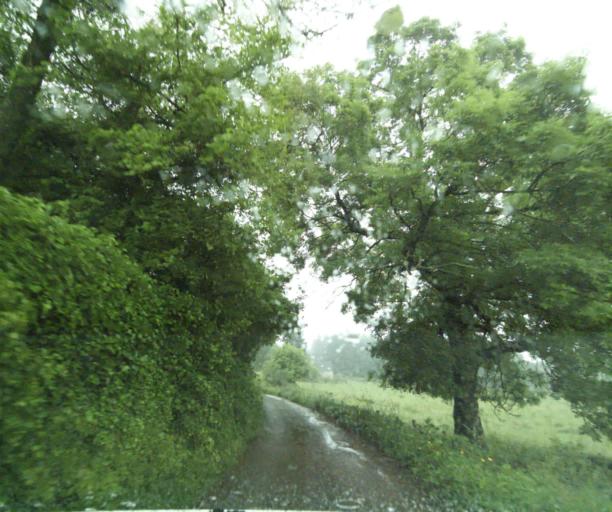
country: FR
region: Bourgogne
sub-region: Departement de Saone-et-Loire
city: La Clayette
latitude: 46.3651
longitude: 4.3502
